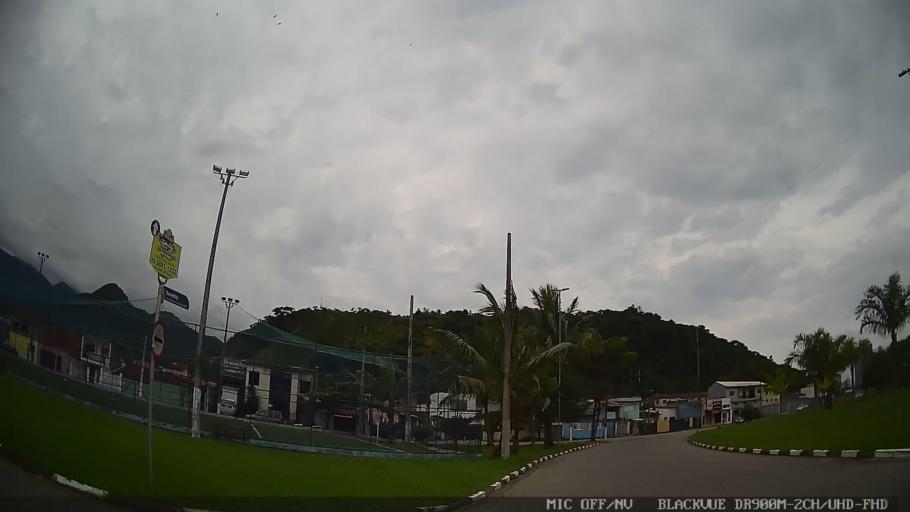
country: BR
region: Sao Paulo
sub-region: Caraguatatuba
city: Caraguatatuba
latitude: -23.6234
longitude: -45.3972
